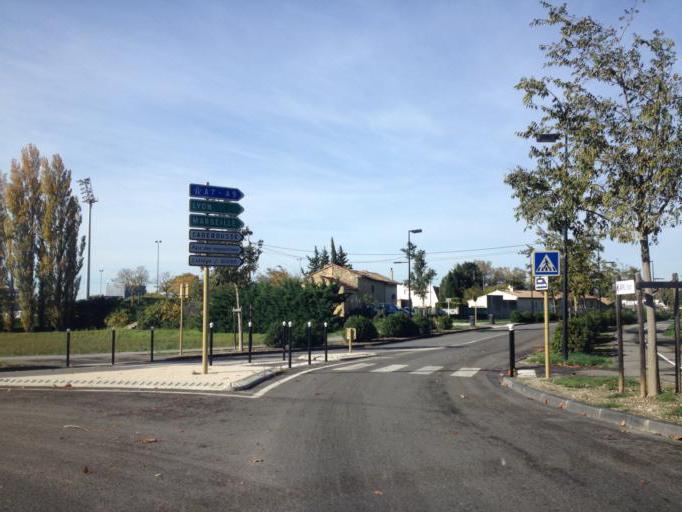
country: FR
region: Provence-Alpes-Cote d'Azur
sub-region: Departement du Vaucluse
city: Orange
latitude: 44.1261
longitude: 4.8012
